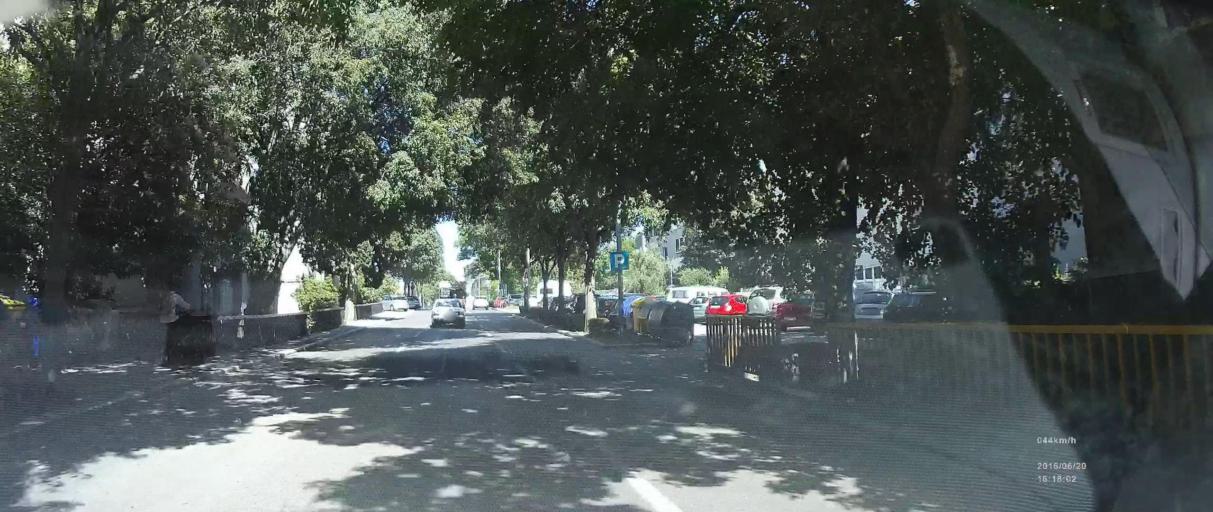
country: HR
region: Splitsko-Dalmatinska
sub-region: Grad Split
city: Split
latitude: 43.5049
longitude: 16.4508
